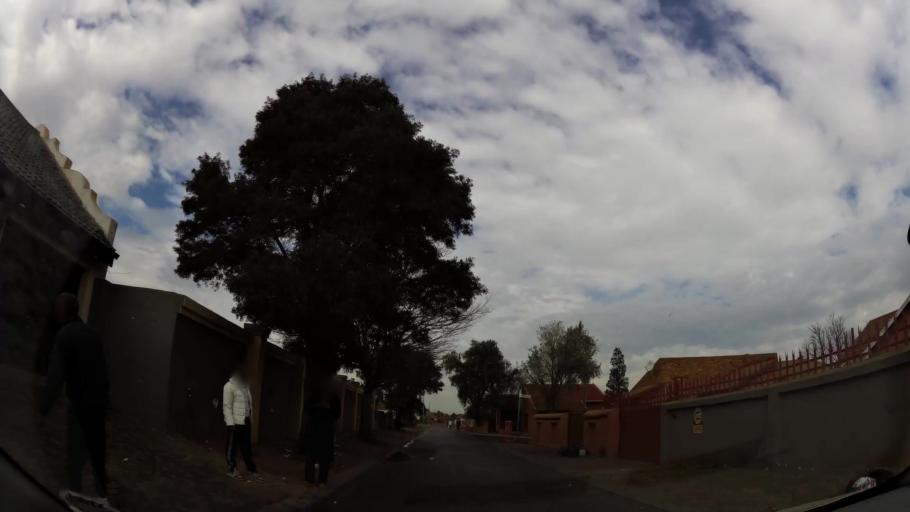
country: ZA
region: Gauteng
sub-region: Ekurhuleni Metropolitan Municipality
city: Germiston
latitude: -26.3232
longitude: 28.1824
